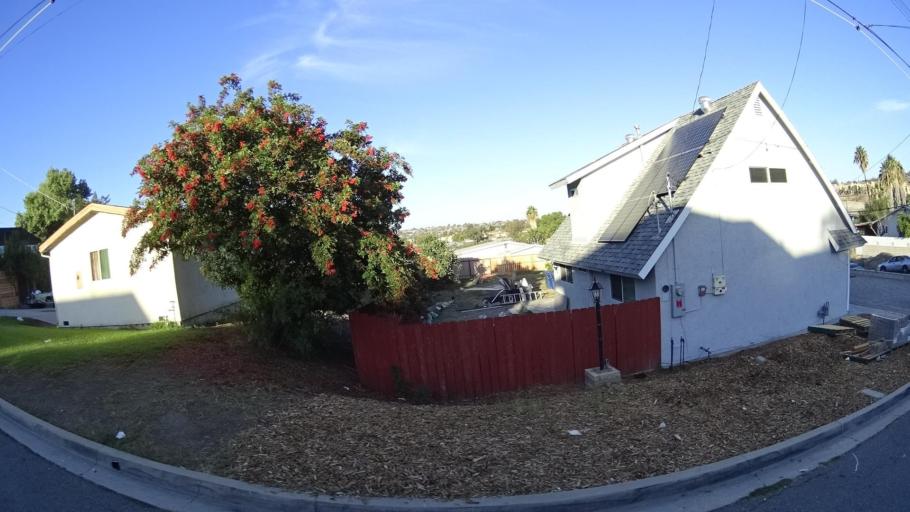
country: US
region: California
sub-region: San Diego County
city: La Presa
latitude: 32.7114
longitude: -117.0009
